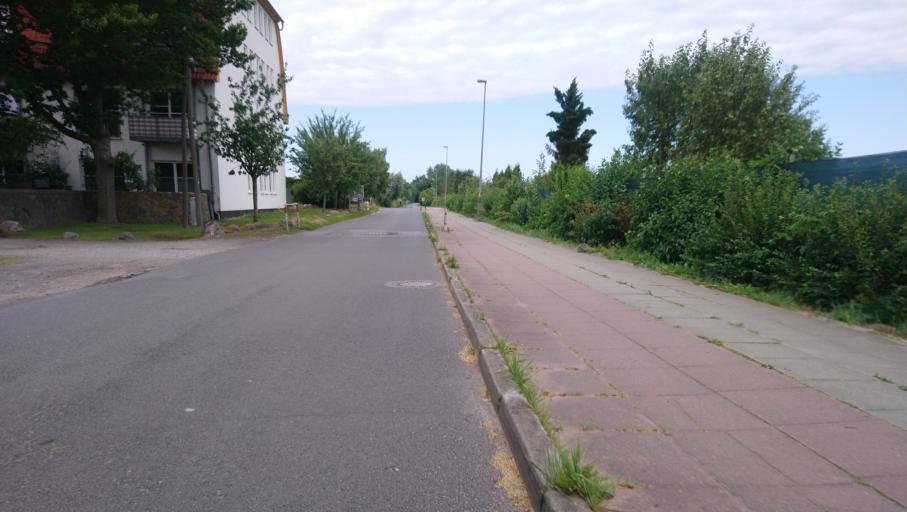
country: DE
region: Mecklenburg-Vorpommern
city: Warnemuende
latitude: 54.1622
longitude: 12.0564
